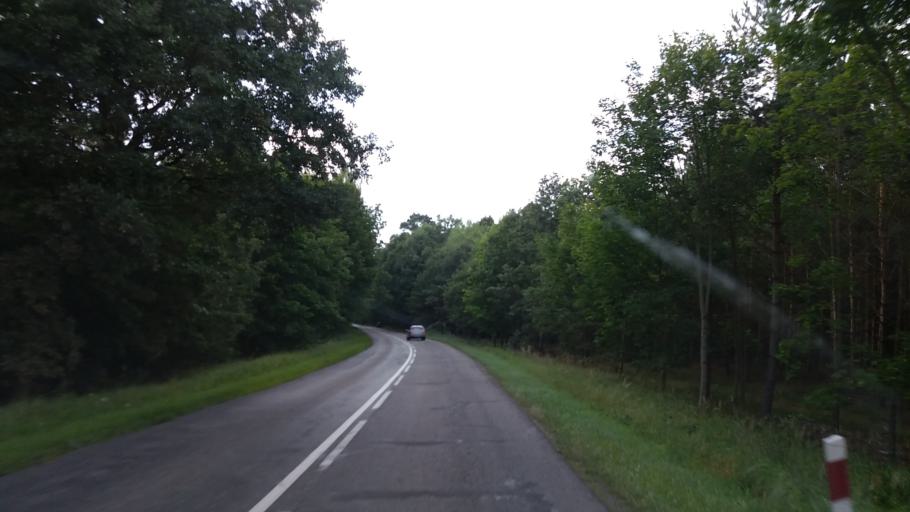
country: PL
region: West Pomeranian Voivodeship
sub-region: Powiat choszczenski
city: Pelczyce
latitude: 53.0684
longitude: 15.2968
